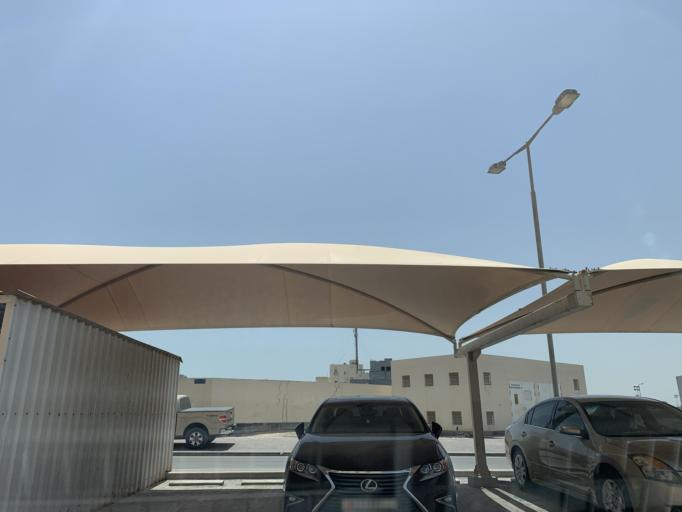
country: BH
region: Northern
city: Sitrah
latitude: 26.1414
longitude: 50.5956
